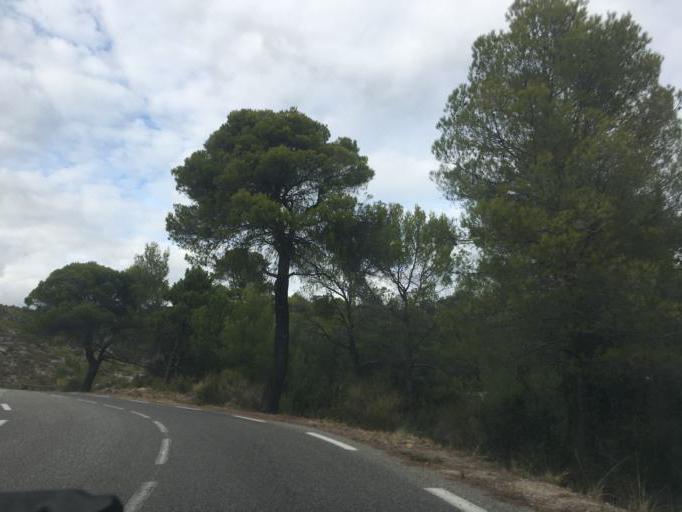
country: FR
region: Provence-Alpes-Cote d'Azur
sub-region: Departement du Var
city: Villecroze
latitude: 43.5866
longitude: 6.2700
